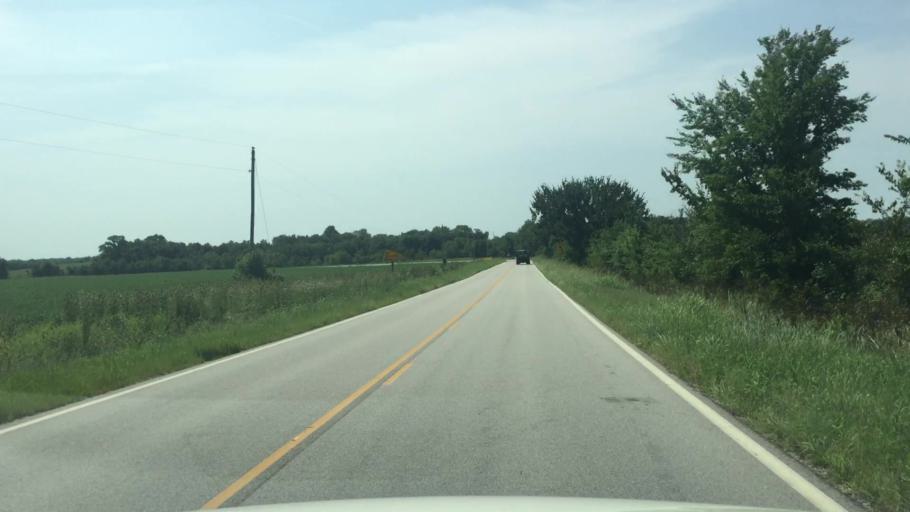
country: US
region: Kansas
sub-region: Montgomery County
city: Cherryvale
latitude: 37.1978
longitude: -95.5580
